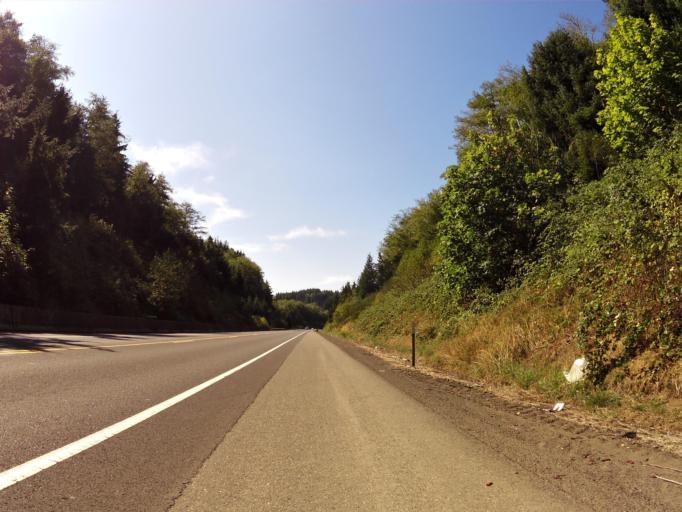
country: US
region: Oregon
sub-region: Clatsop County
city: Astoria
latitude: 46.1683
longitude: -123.6891
